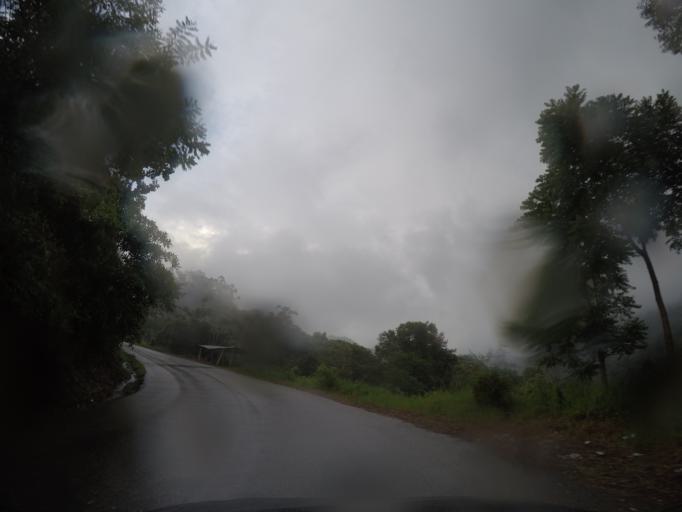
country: MX
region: Oaxaca
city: San Gabriel Mixtepec
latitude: 16.0776
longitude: -97.0883
